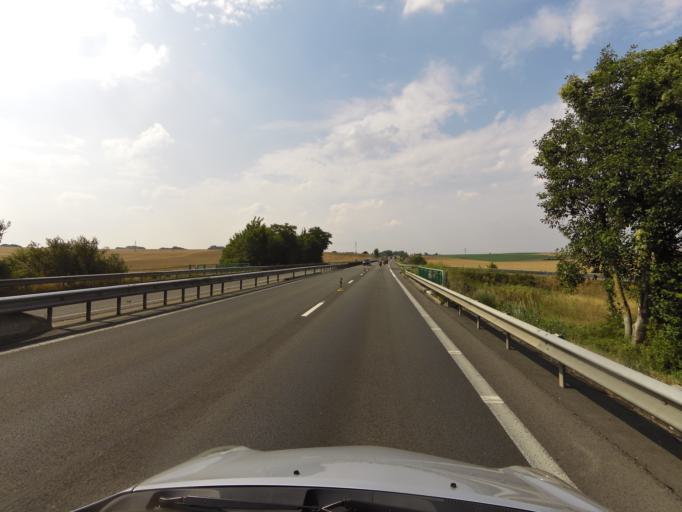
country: FR
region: Picardie
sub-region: Departement de l'Aisne
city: Itancourt
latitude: 49.7586
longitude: 3.3690
